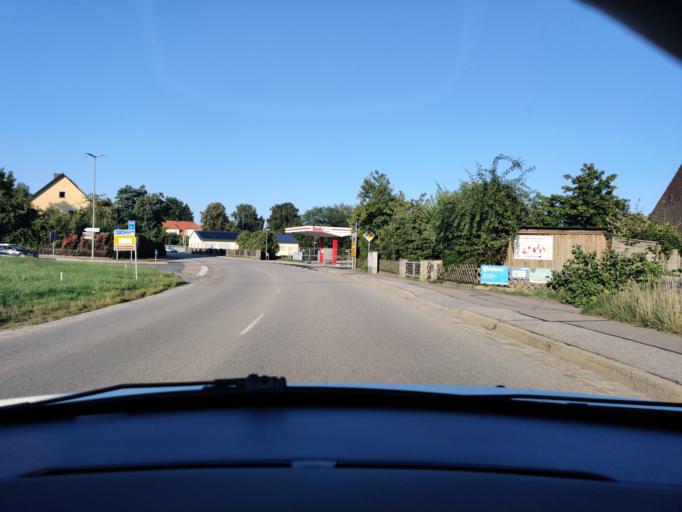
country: DE
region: Bavaria
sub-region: Upper Palatinate
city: Nabburg
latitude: 49.4476
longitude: 12.1746
